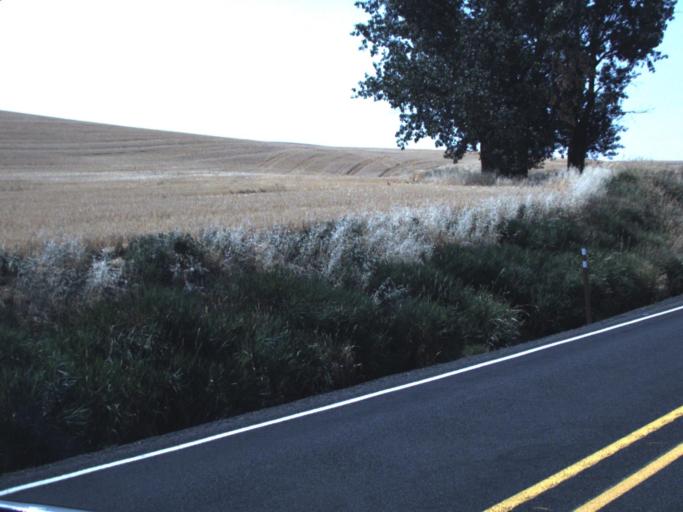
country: US
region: Washington
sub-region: Whitman County
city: Pullman
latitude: 46.9630
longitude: -117.0995
